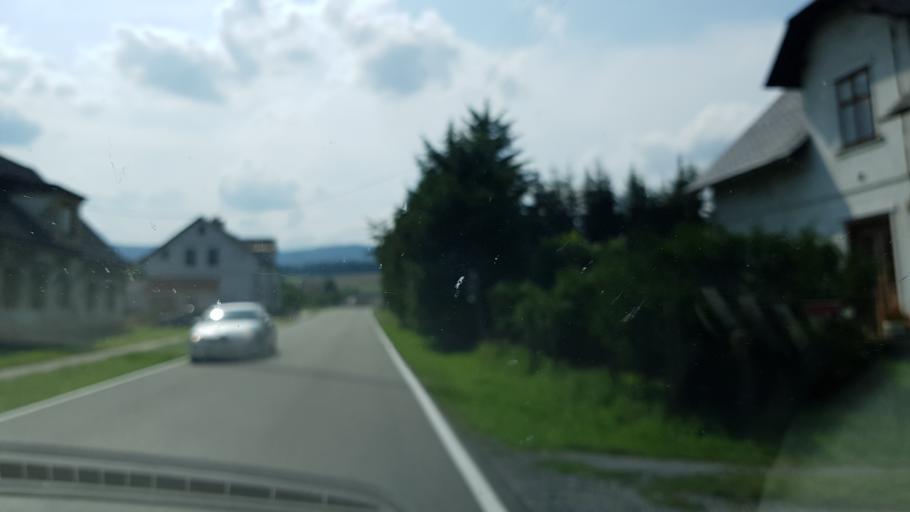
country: CZ
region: Olomoucky
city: Pisecna
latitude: 50.2782
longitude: 17.2821
